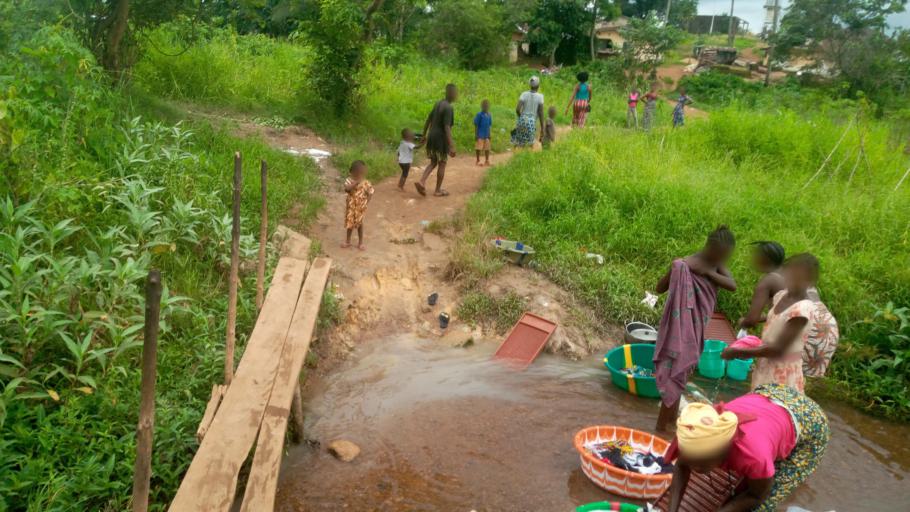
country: SL
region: Southern Province
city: Mogbwemo
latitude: 7.6030
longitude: -12.1792
